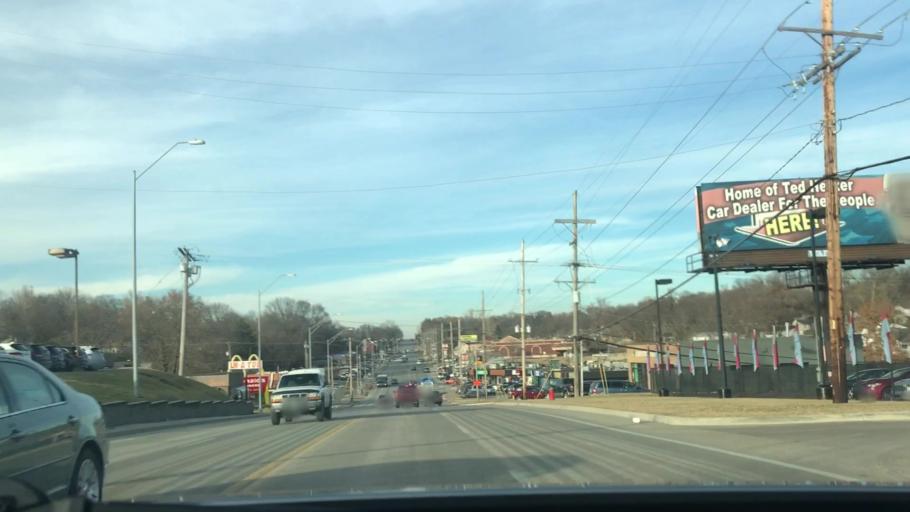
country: US
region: Missouri
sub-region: Platte County
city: Riverside
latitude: 39.1661
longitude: -94.5768
